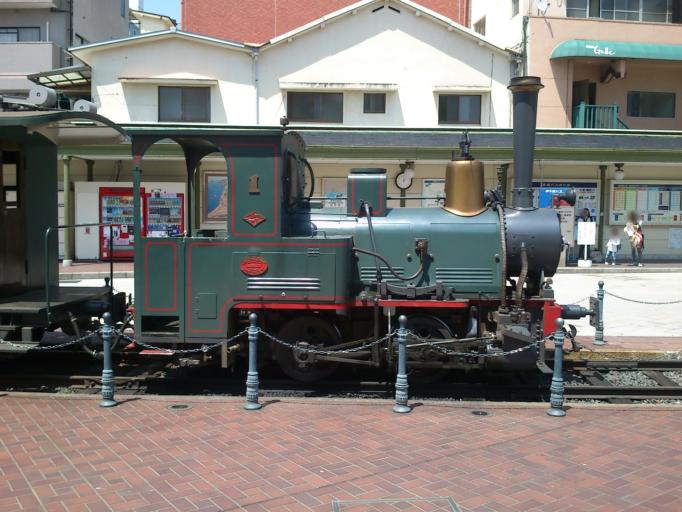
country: JP
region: Ehime
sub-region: Shikoku-chuo Shi
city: Matsuyama
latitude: 33.8508
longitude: 132.7859
